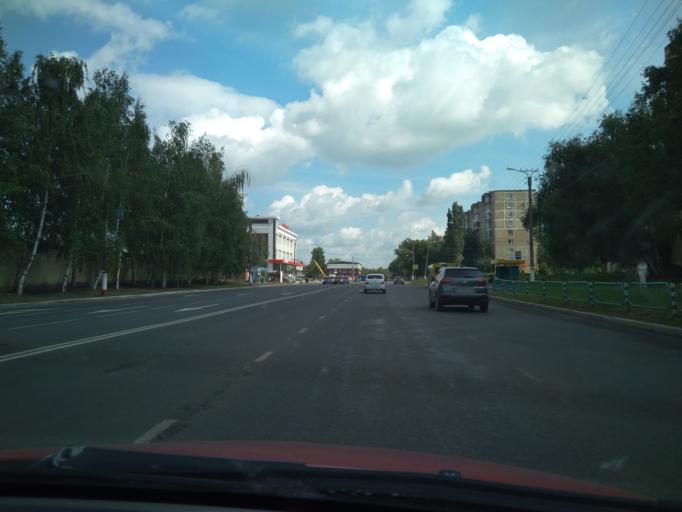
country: RU
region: Mordoviya
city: Saransk
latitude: 54.1993
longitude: 45.2268
